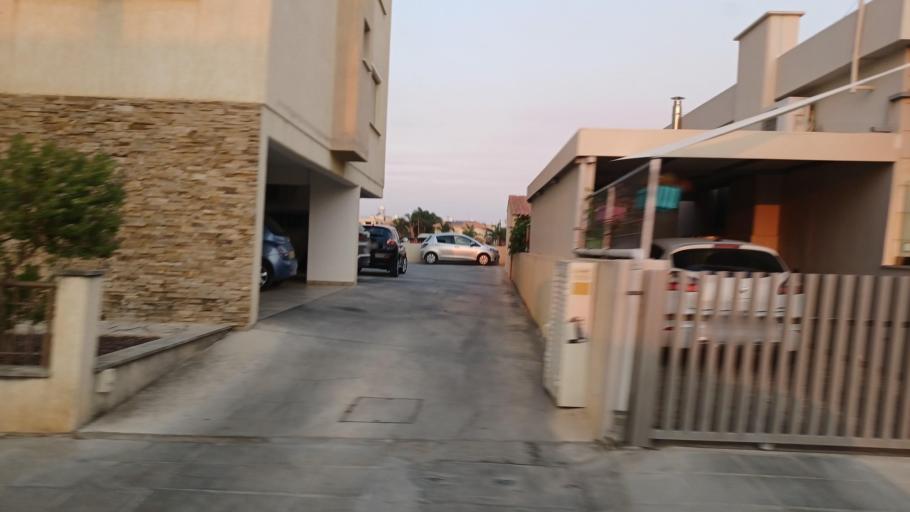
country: CY
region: Limassol
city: Pano Polemidia
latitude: 34.6835
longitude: 33.0051
